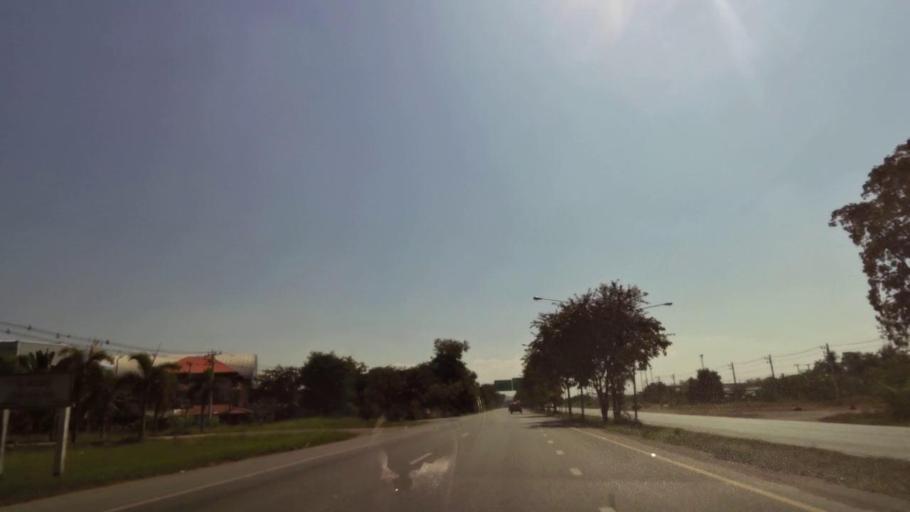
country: TH
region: Nakhon Sawan
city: Nakhon Sawan
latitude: 15.7739
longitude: 100.1214
